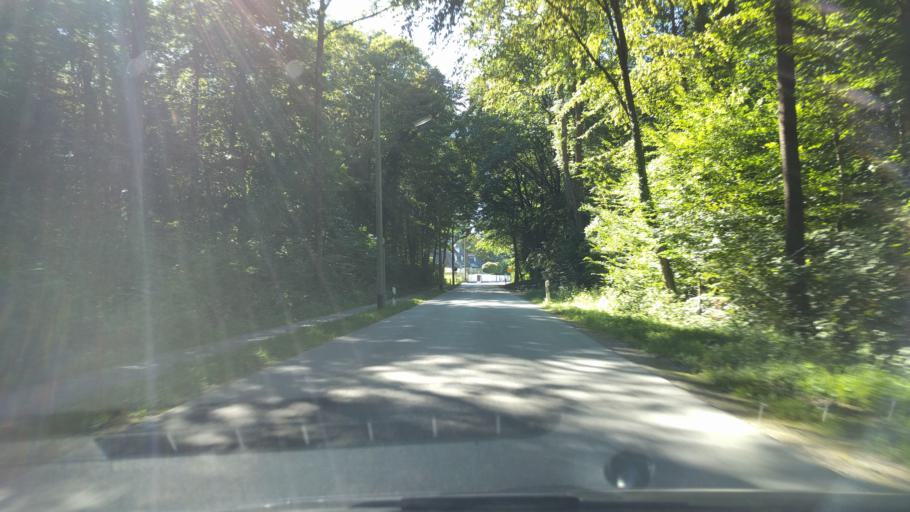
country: DE
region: Bavaria
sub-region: Upper Bavaria
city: Grunwald
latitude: 48.0394
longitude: 11.5424
